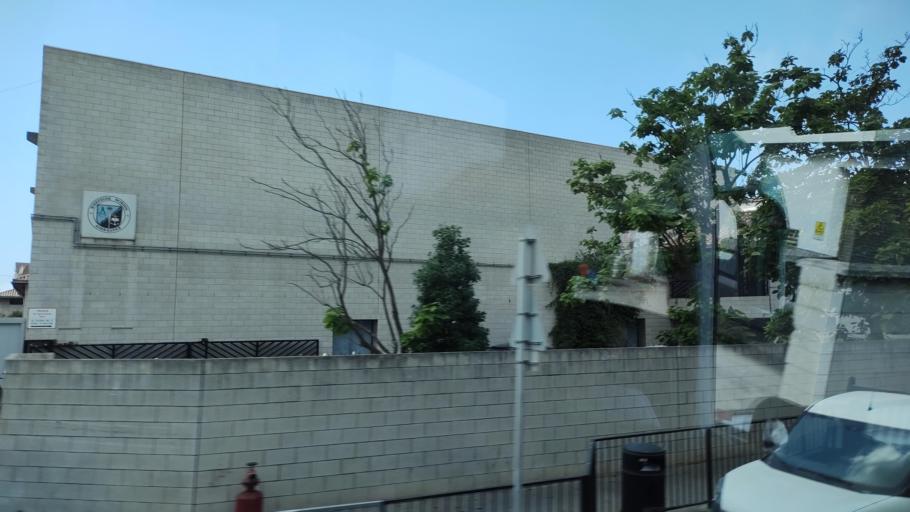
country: GI
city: Gibraltar
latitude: 36.1439
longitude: -5.3549
